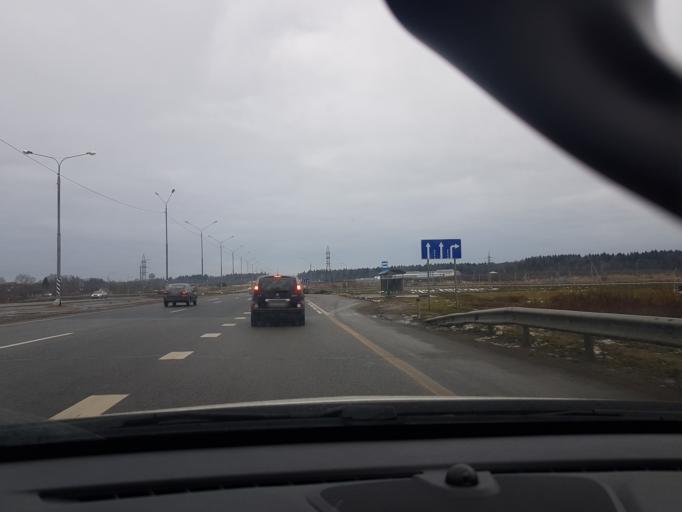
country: RU
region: Moskovskaya
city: Sychevo
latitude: 55.9944
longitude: 36.2325
